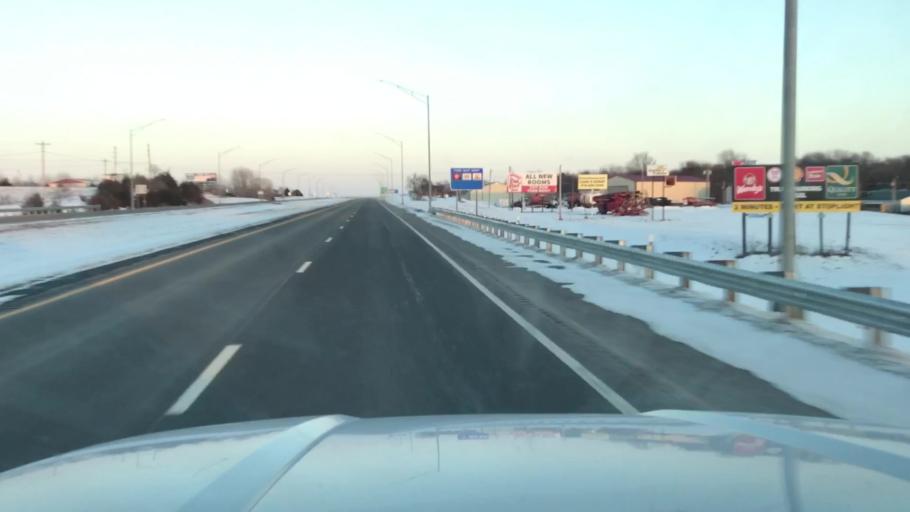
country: US
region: Missouri
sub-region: Clinton County
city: Cameron
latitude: 39.7539
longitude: -94.2467
